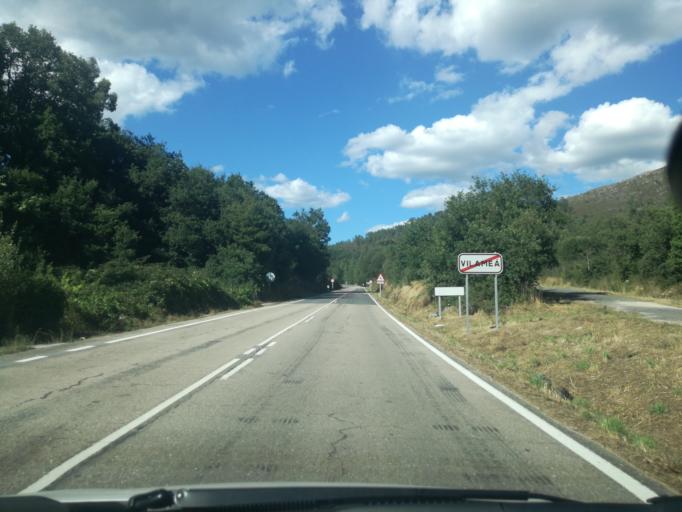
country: ES
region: Galicia
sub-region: Provincia de Ourense
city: Lobios
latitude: 41.8752
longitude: -8.0990
